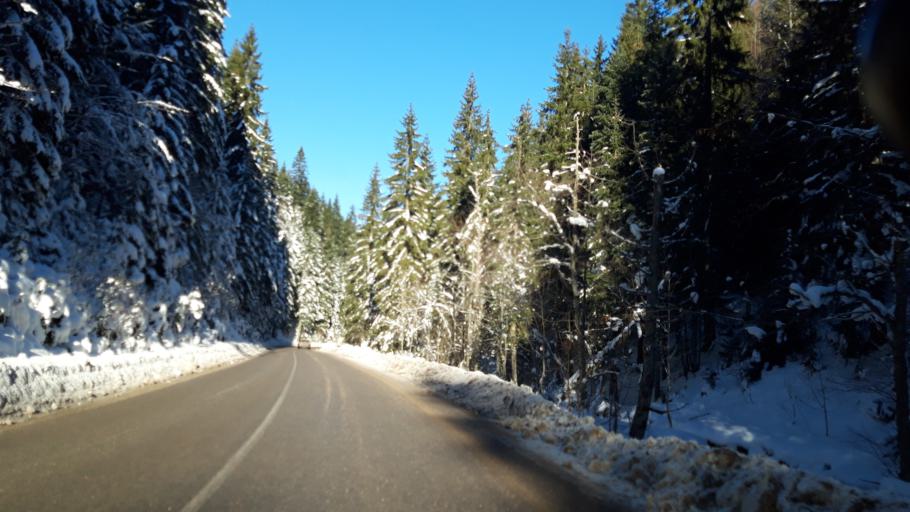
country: BA
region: Republika Srpska
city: Koran
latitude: 43.7529
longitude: 18.5504
